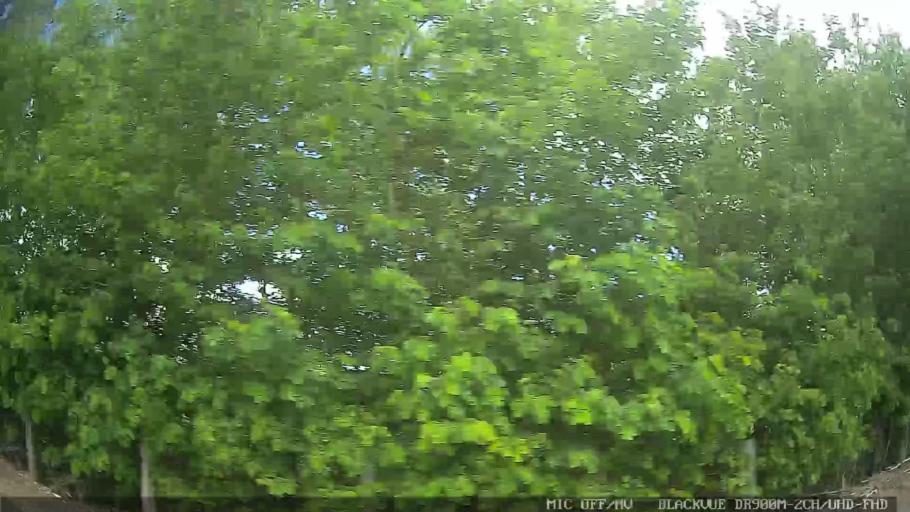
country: BR
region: Sao Paulo
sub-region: Conchas
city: Conchas
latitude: -22.9852
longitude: -47.9913
